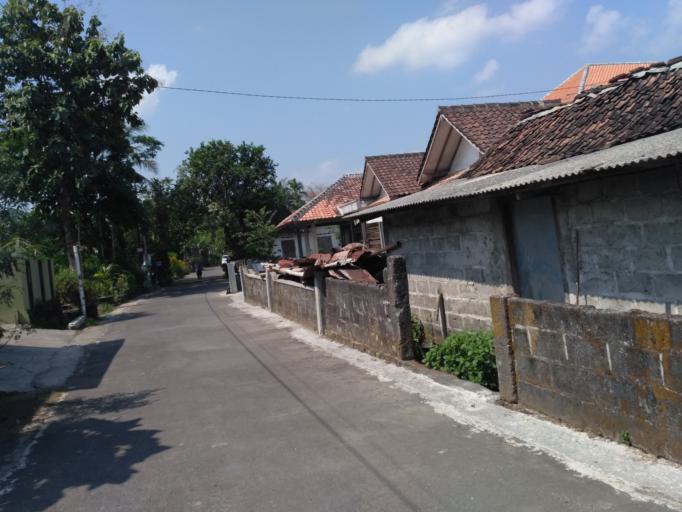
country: ID
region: Daerah Istimewa Yogyakarta
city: Depok
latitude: -7.7076
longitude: 110.4174
